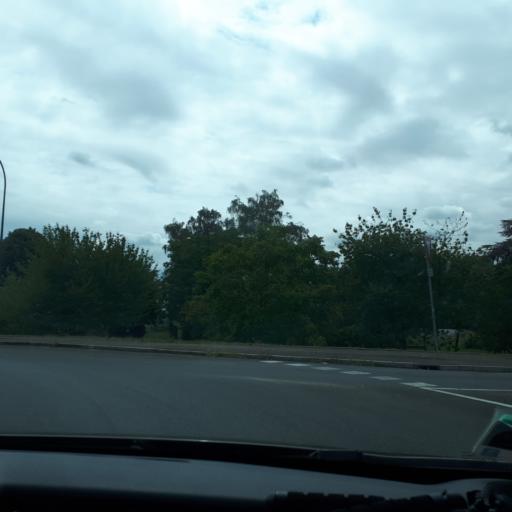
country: FR
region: Centre
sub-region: Departement du Loiret
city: Saint-Pere-sur-Loire
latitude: 47.7725
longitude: 2.3716
